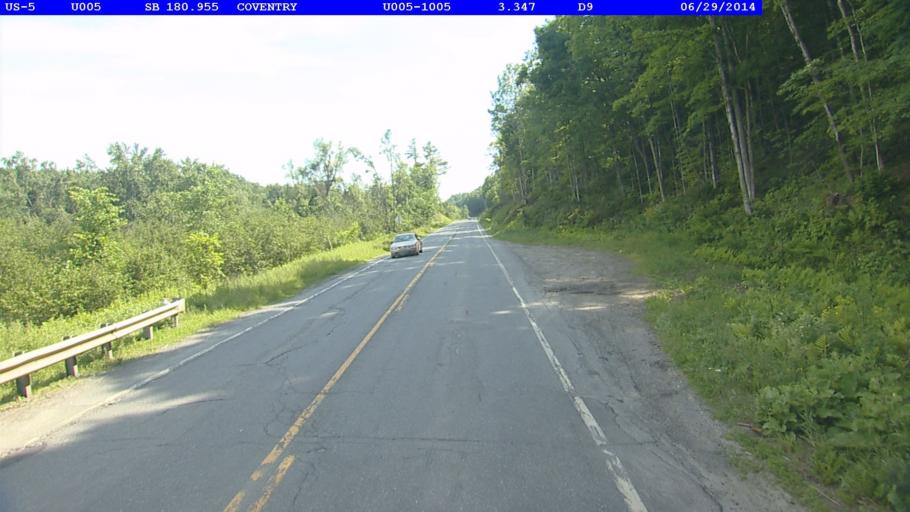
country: US
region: Vermont
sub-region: Orleans County
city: Newport
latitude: 44.9028
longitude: -72.2429
